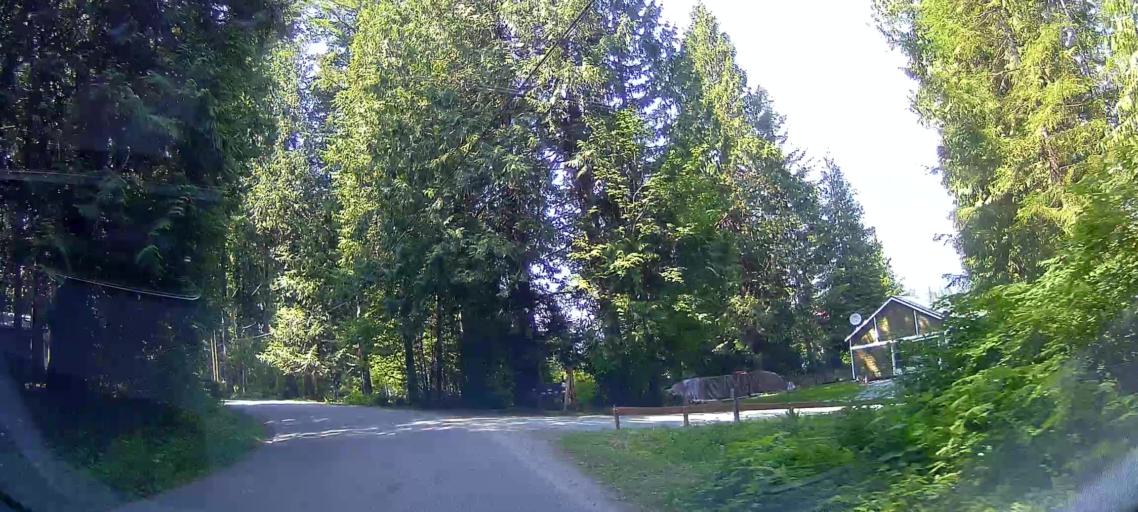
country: US
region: Washington
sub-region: Snohomish County
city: Arlington Heights
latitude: 48.3173
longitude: -122.0168
